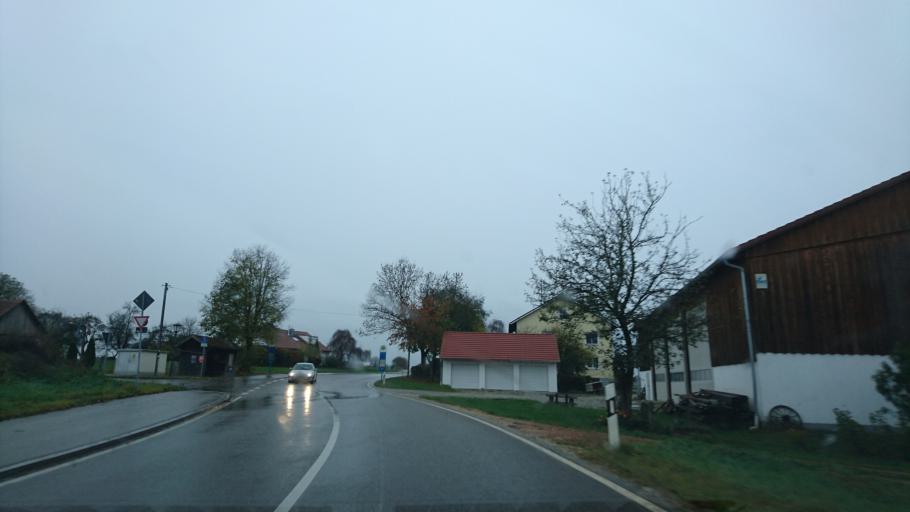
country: DE
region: Bavaria
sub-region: Upper Bavaria
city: Hilgertshausen-Tandern
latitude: 48.4315
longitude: 11.3428
